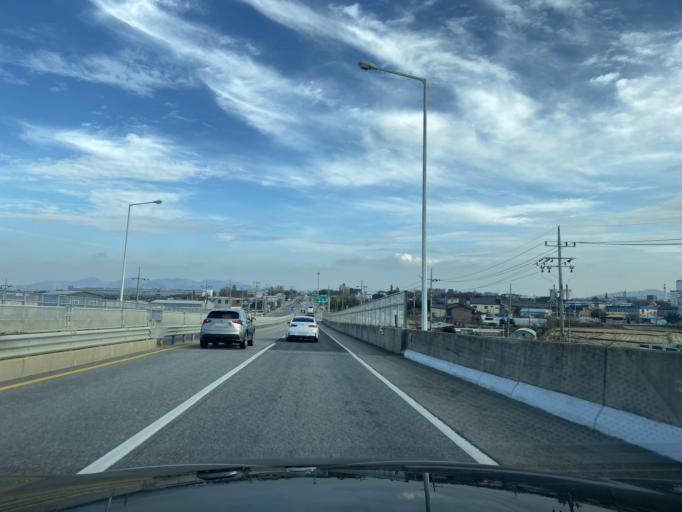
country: KR
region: Chungcheongnam-do
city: Yesan
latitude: 36.6909
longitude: 126.7398
